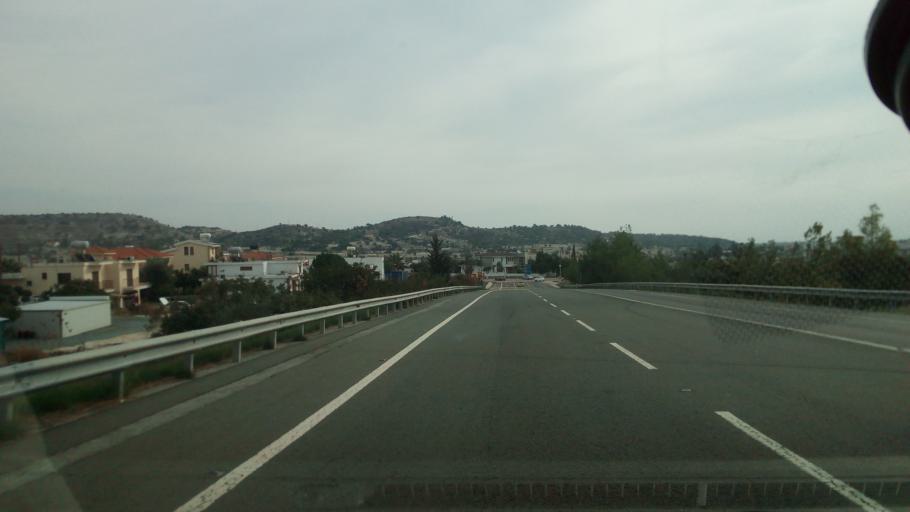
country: CY
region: Larnaka
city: Tersefanou
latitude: 34.8682
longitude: 33.4954
